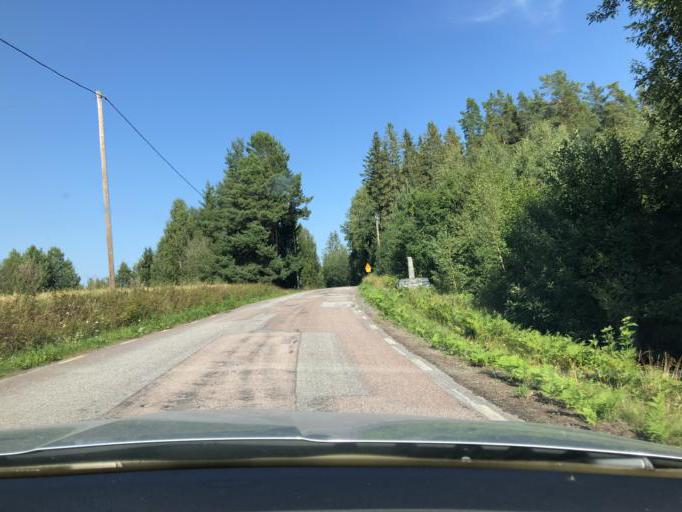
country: SE
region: Dalarna
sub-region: Hedemora Kommun
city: Hedemora
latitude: 60.3262
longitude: 15.9143
